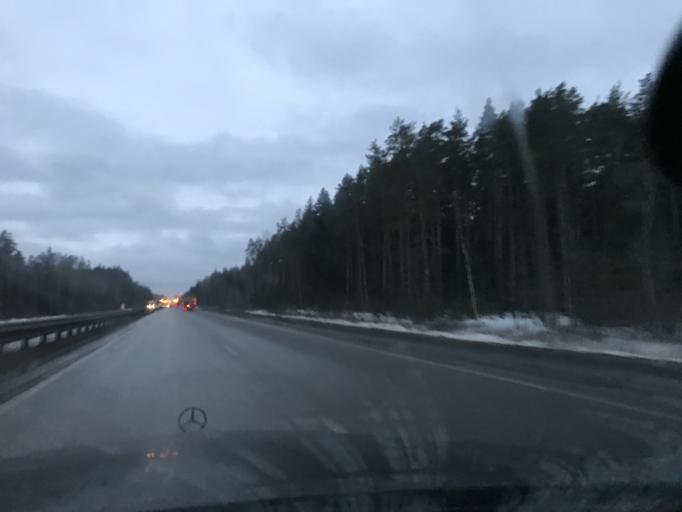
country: RU
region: Vladimir
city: Petushki
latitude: 55.9294
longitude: 39.3423
